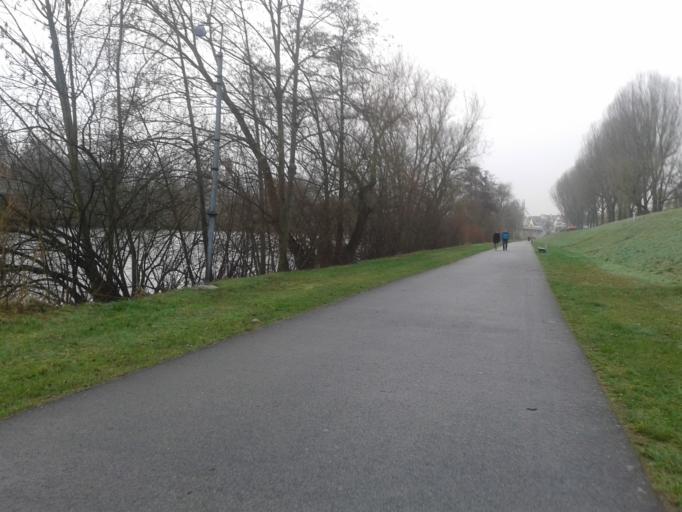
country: DE
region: Bavaria
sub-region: Upper Franconia
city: Bamberg
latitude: 49.9004
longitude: 10.8815
